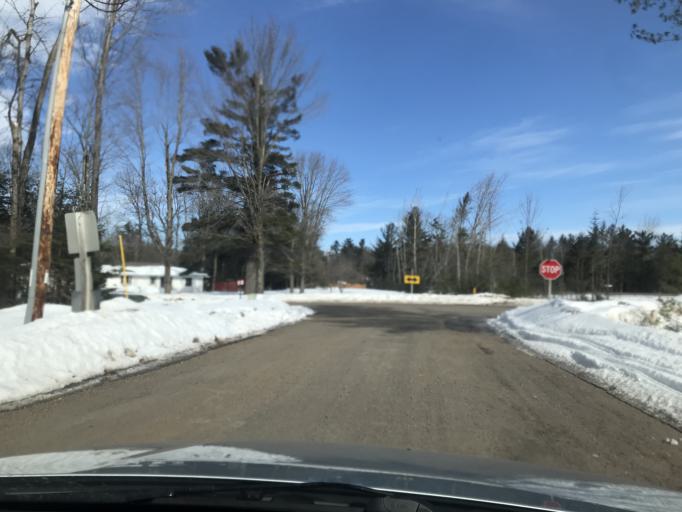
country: US
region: Wisconsin
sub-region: Oconto County
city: Gillett
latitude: 45.1249
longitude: -88.4193
